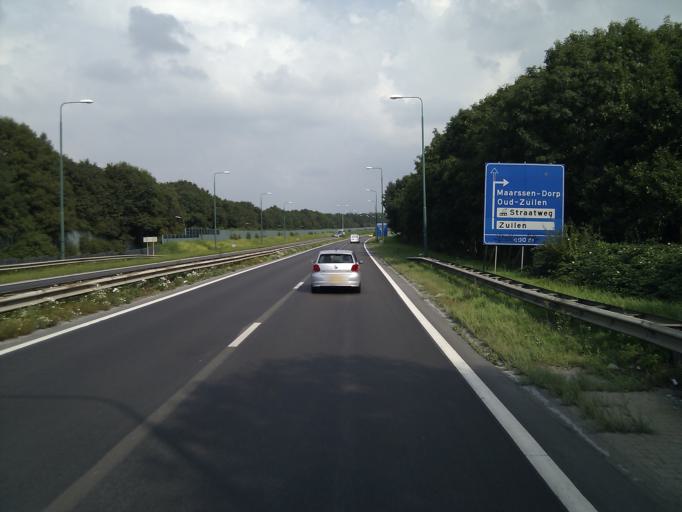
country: NL
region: Utrecht
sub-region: Stichtse Vecht
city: Maarssen
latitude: 52.1313
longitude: 5.0499
